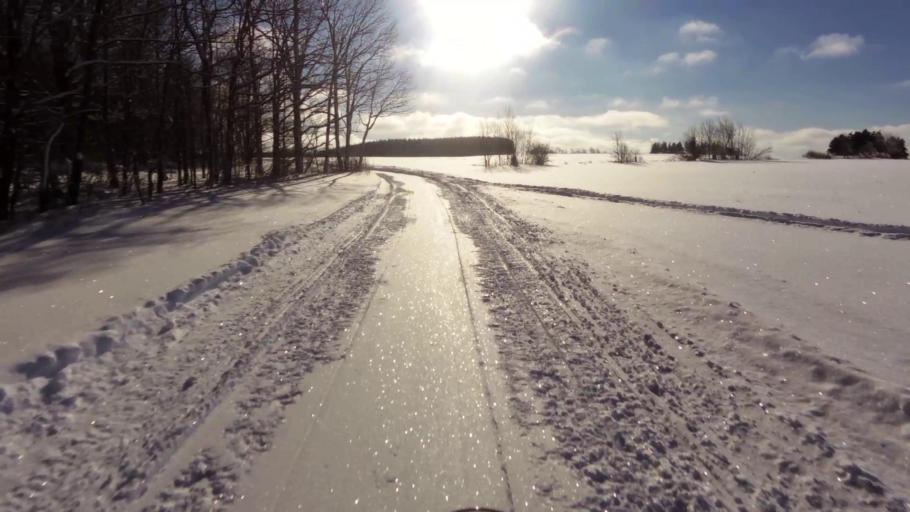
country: US
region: New York
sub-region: Chautauqua County
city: Falconer
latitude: 42.2685
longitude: -79.1903
